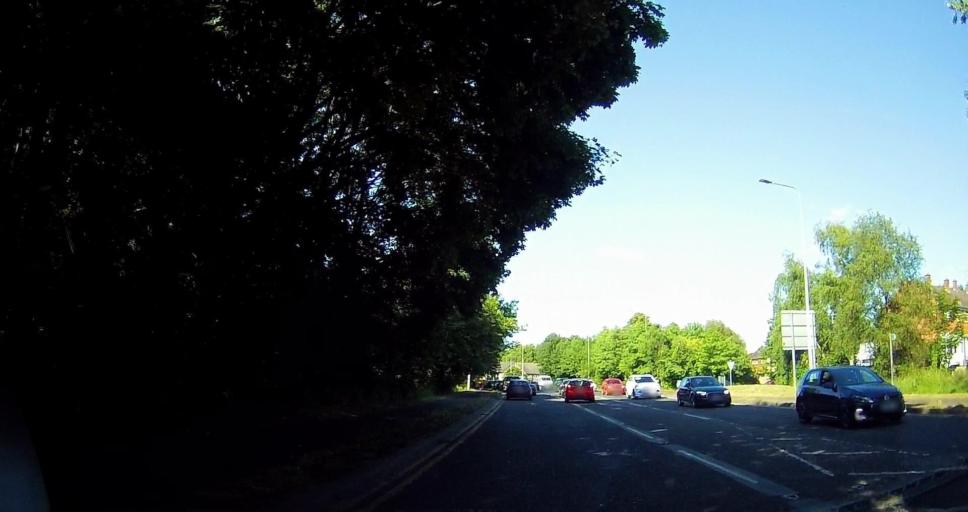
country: GB
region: England
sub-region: Cheshire East
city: Sandbach
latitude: 53.1414
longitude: -2.3602
